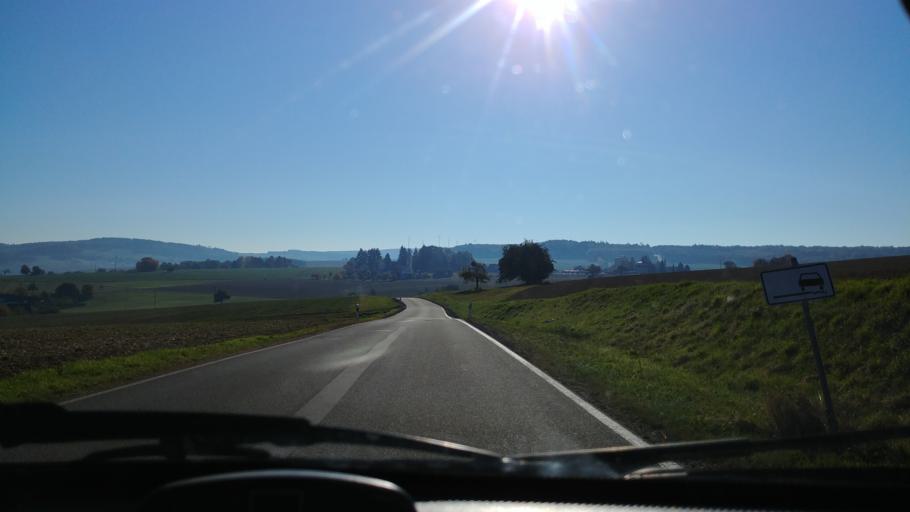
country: DE
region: Rheinland-Pfalz
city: Lollschied
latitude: 50.2564
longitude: 7.8598
